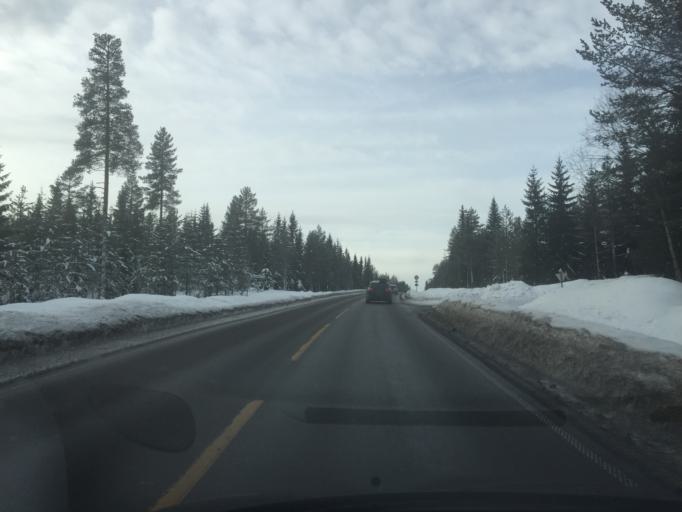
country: NO
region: Hedmark
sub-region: Trysil
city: Innbygda
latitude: 61.2470
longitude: 12.2927
